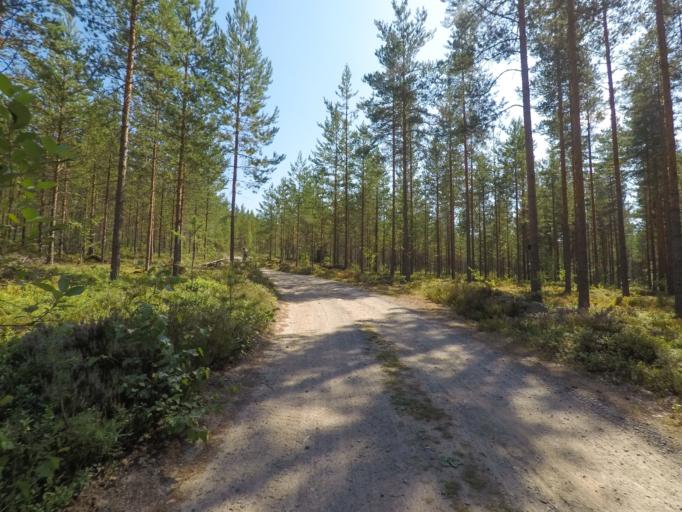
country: FI
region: Southern Savonia
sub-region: Mikkeli
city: Puumala
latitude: 61.4296
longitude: 28.0058
